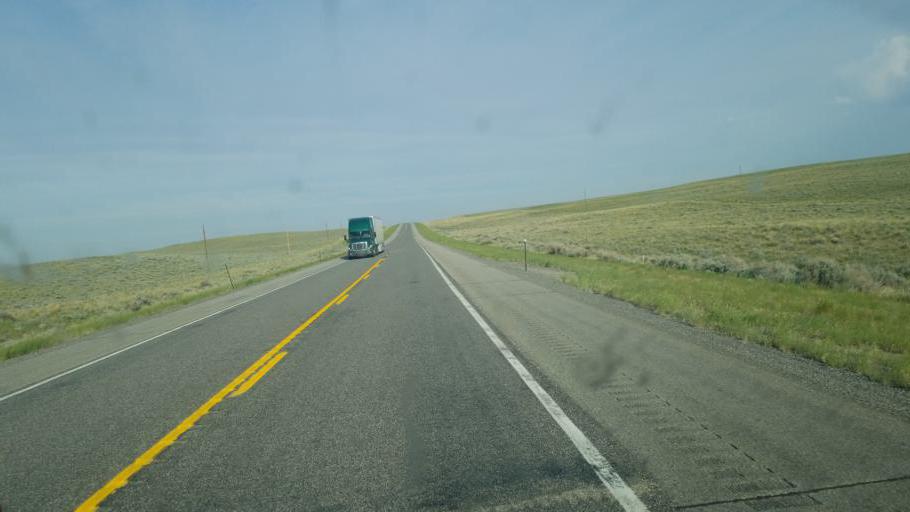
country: US
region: Wyoming
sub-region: Hot Springs County
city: Thermopolis
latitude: 43.1406
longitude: -107.4616
